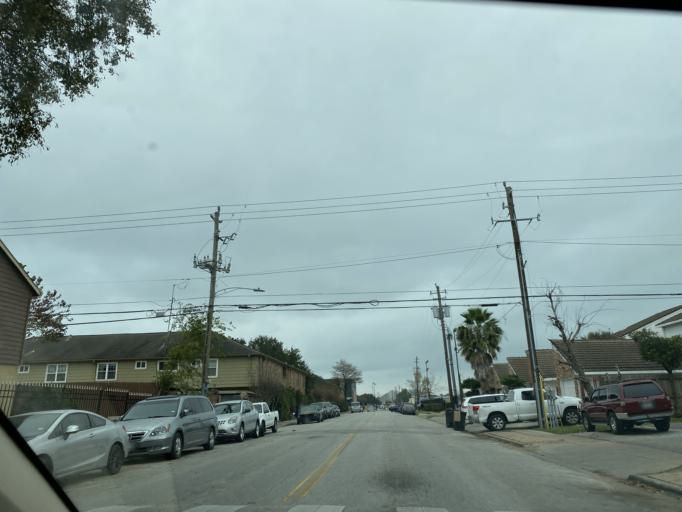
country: US
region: Texas
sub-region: Harris County
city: Piney Point Village
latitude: 29.7268
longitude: -95.4979
